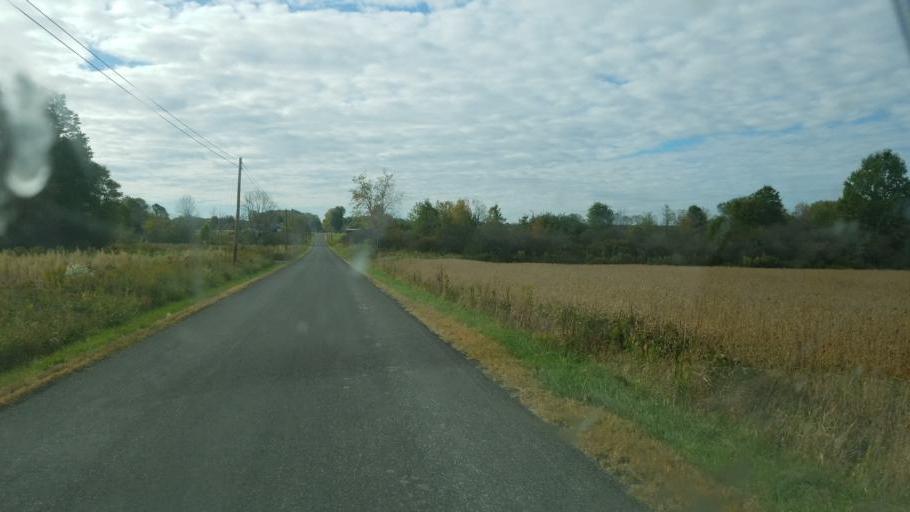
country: US
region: Pennsylvania
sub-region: Mercer County
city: Reynolds Heights
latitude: 41.3341
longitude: -80.2863
